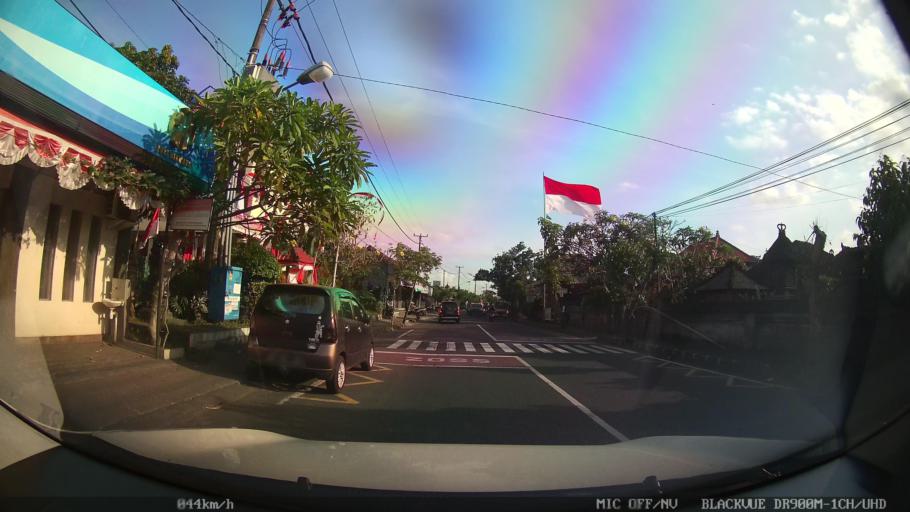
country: ID
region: Bali
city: Banjar Kertasari
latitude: -8.6163
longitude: 115.2124
